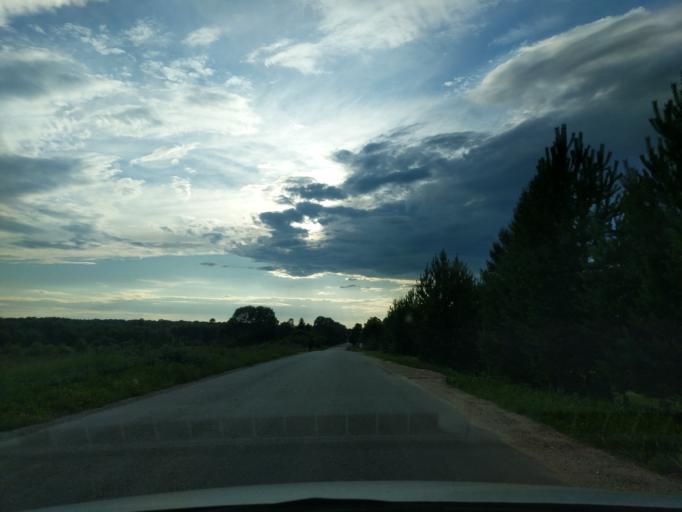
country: RU
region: Kaluga
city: Myatlevo
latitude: 54.8301
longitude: 35.6501
